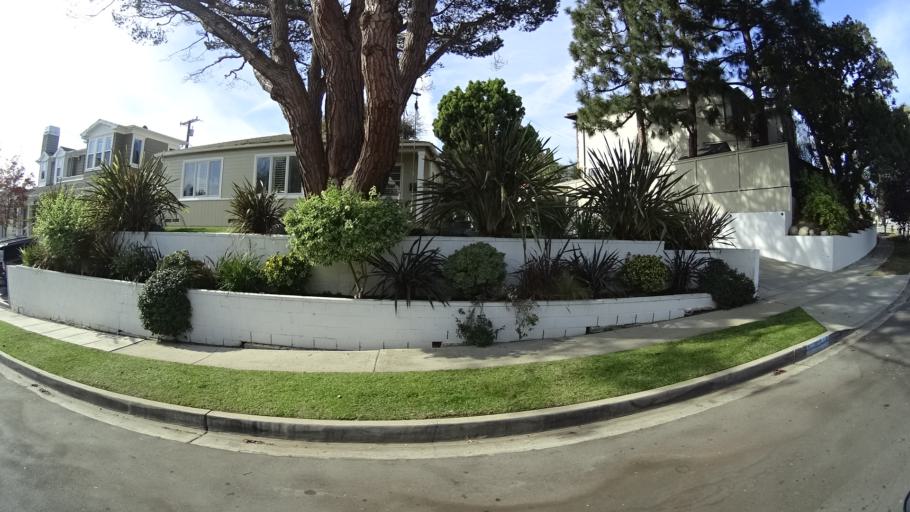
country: US
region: California
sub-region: Los Angeles County
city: Manhattan Beach
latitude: 33.8920
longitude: -118.3926
